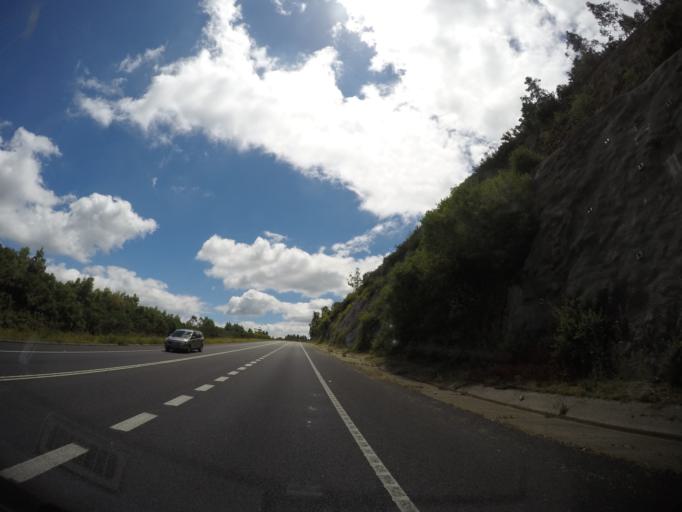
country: ES
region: Aragon
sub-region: Provincia de Zaragoza
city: El Burgo de Ebro
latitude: 41.5431
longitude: -0.7365
